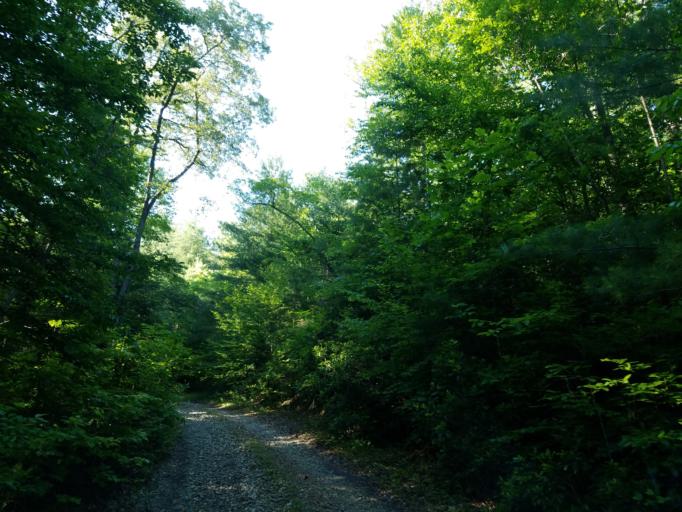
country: US
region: Georgia
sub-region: Fannin County
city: Blue Ridge
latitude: 34.8024
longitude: -84.1844
